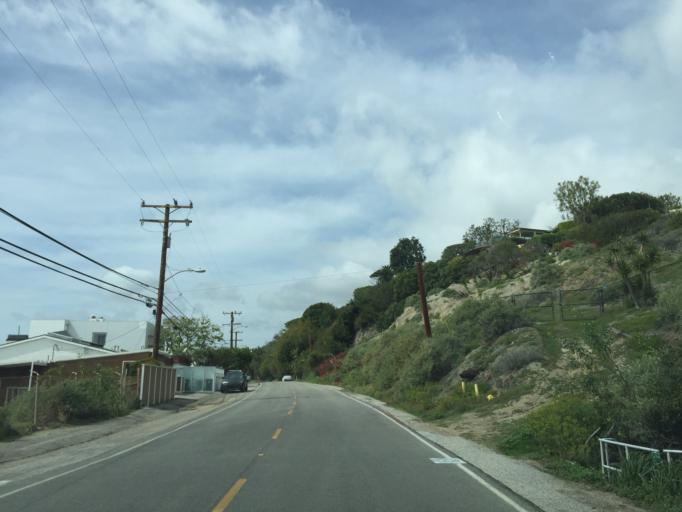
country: US
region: California
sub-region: Los Angeles County
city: Malibu Beach
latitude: 34.0318
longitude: -118.7140
